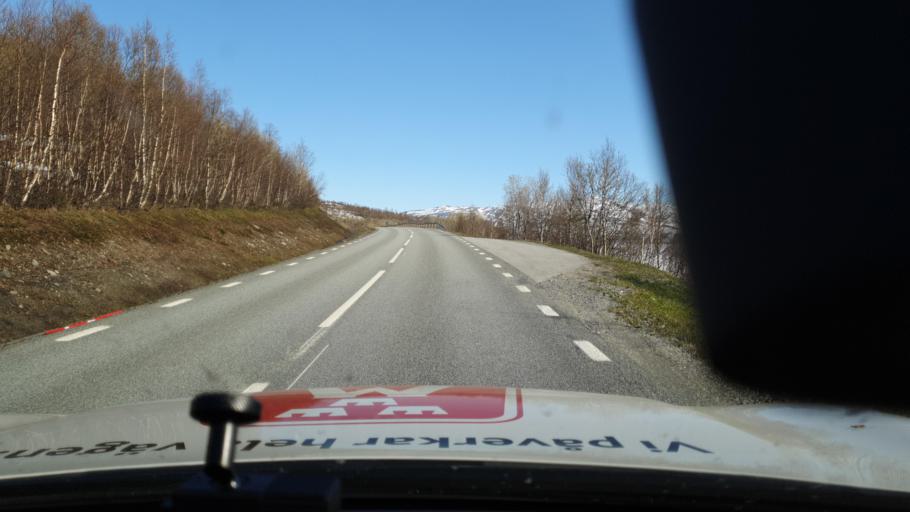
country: NO
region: Nordland
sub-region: Rana
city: Mo i Rana
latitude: 66.1109
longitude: 14.8143
